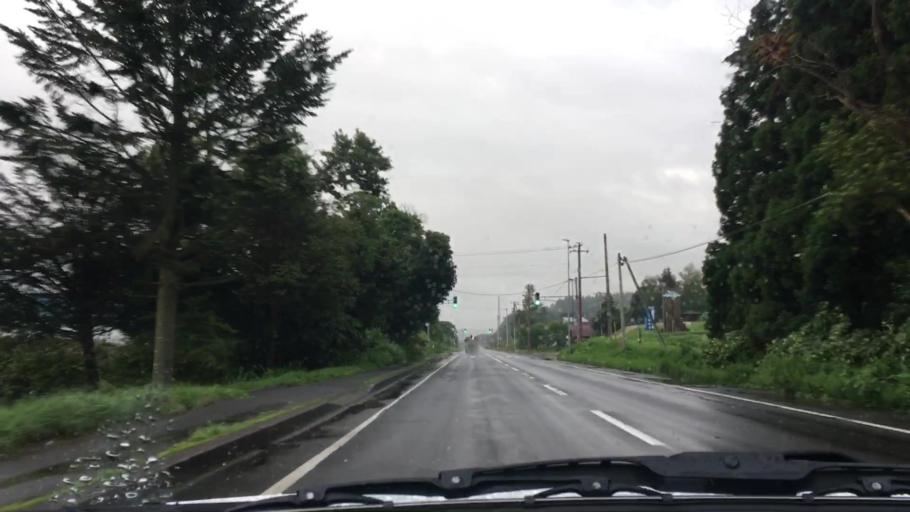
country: JP
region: Hokkaido
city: Nanae
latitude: 42.1758
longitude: 140.4522
